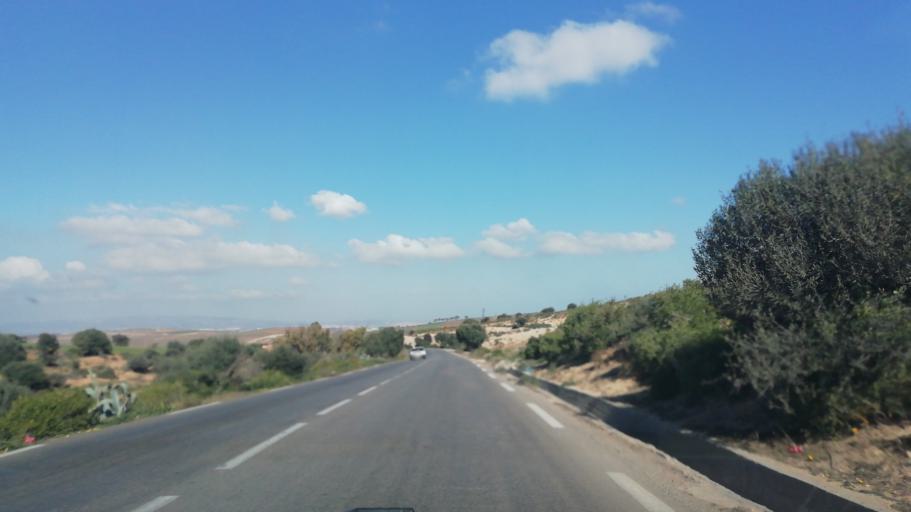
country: DZ
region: Oran
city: Ain el Bya
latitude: 35.7254
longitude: -0.2456
